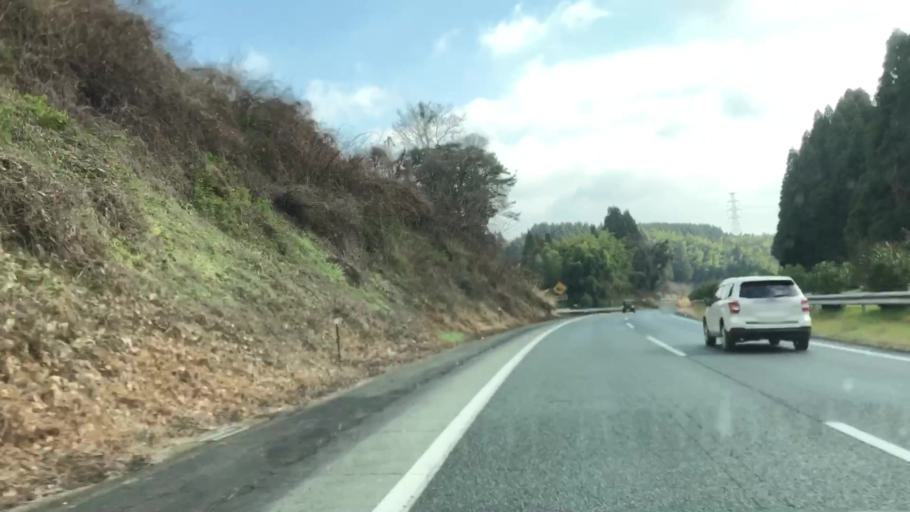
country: JP
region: Fukuoka
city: Omuta
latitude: 33.0424
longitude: 130.5674
